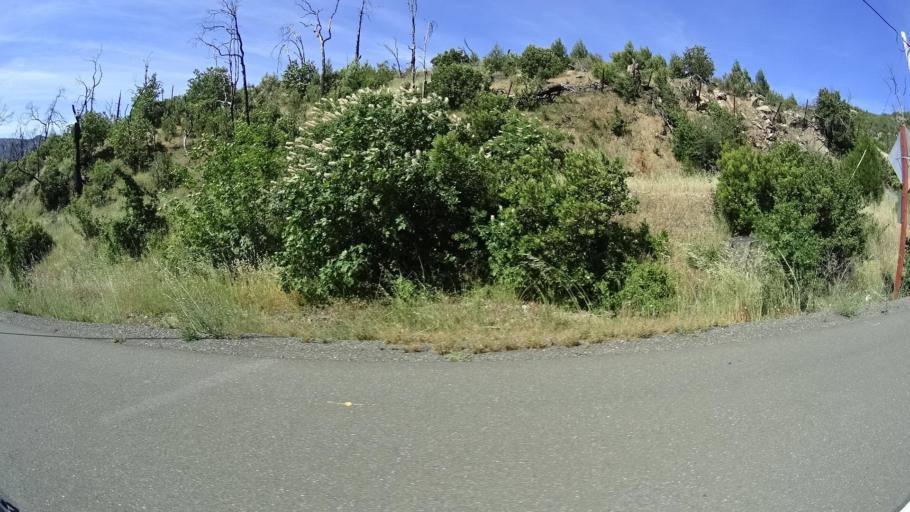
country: US
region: California
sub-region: Lake County
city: Cobb
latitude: 38.7886
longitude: -122.6943
